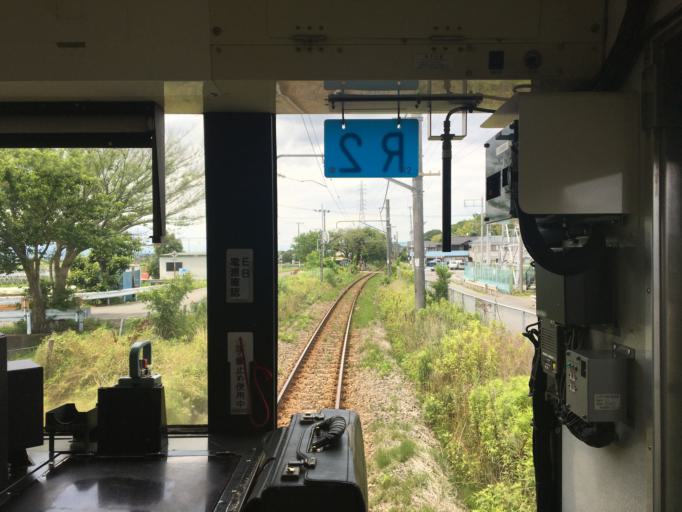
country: JP
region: Kanagawa
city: Zama
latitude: 35.4952
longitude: 139.3861
